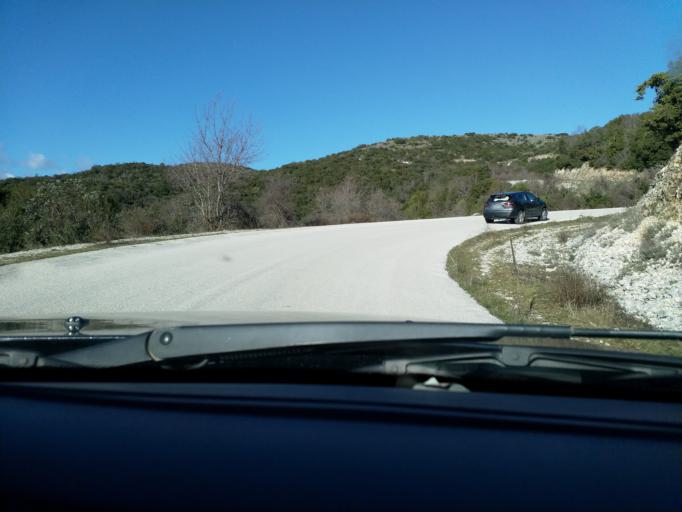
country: GR
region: Epirus
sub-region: Nomos Ioanninon
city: Kalpaki
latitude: 39.9033
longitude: 20.6722
